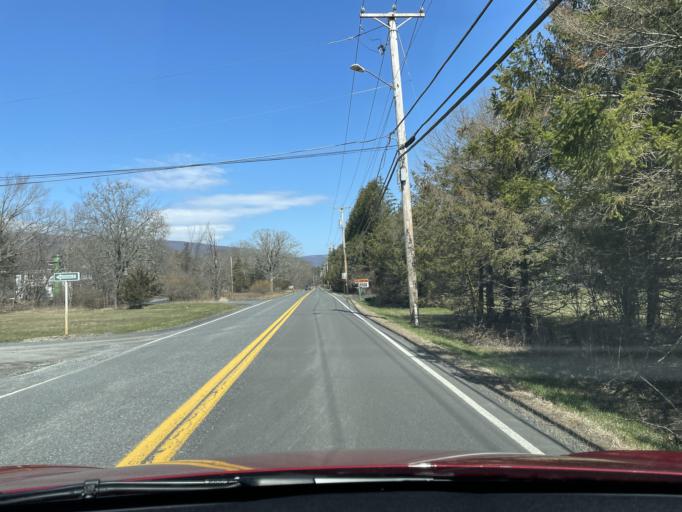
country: US
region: New York
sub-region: Ulster County
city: Manorville
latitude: 42.0923
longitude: -74.0176
